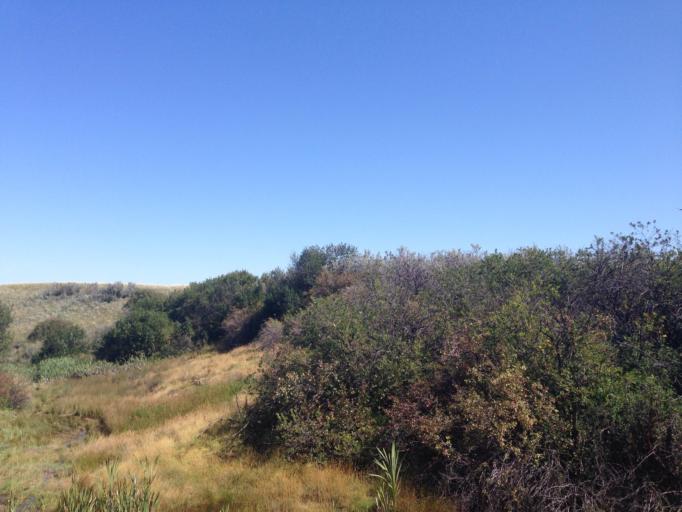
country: CA
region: Alberta
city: Medicine Hat
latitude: 50.0154
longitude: -110.6281
